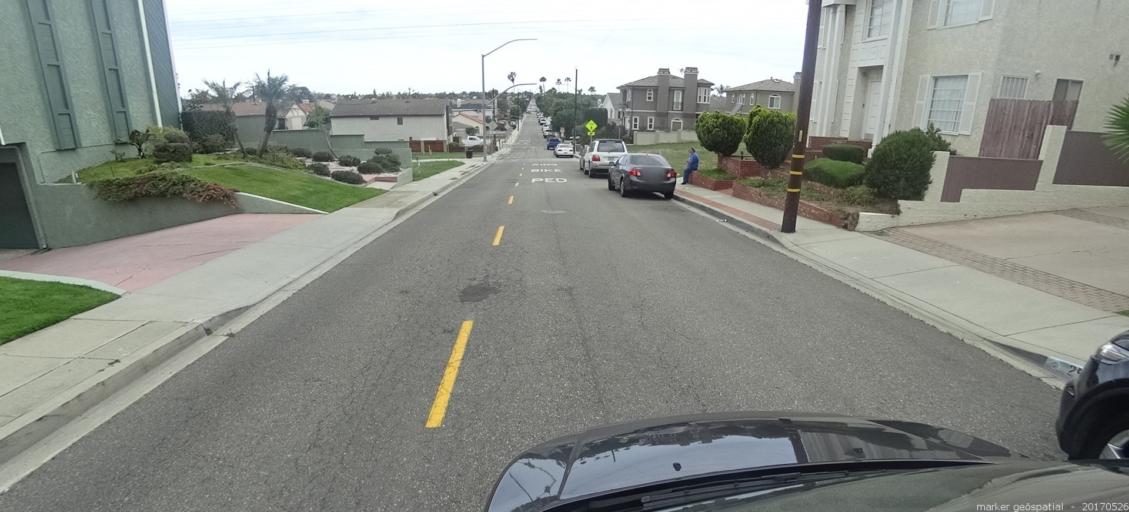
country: US
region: California
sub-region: Los Angeles County
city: Lawndale
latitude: 33.8766
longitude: -118.3653
